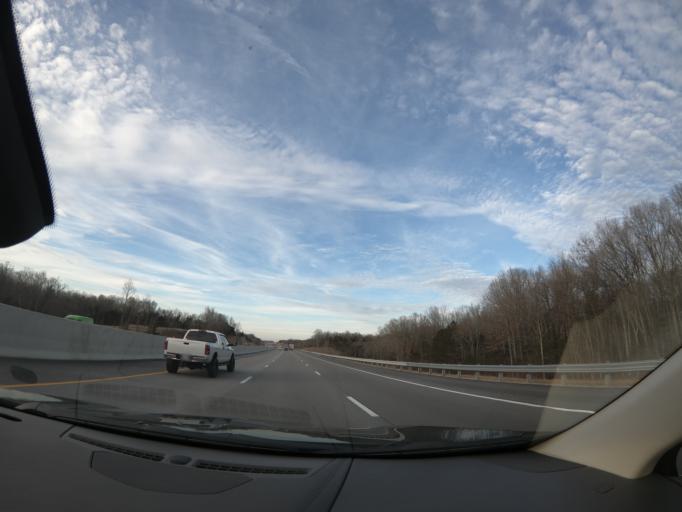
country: US
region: Kentucky
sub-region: Hart County
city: Munfordville
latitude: 37.4084
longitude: -85.8813
